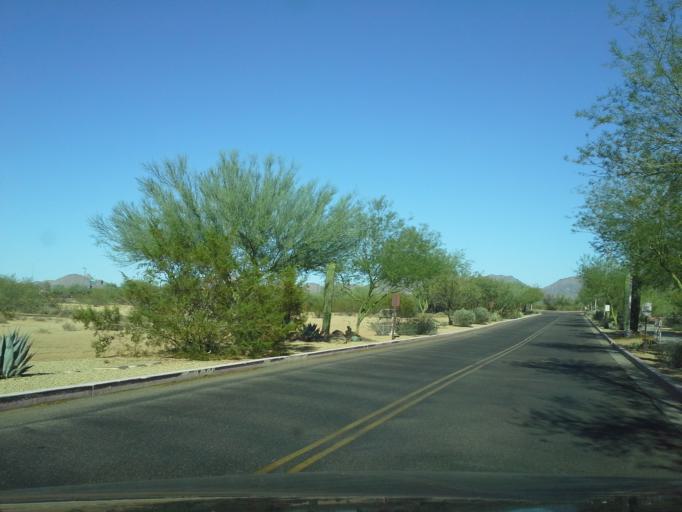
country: US
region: Arizona
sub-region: Maricopa County
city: Paradise Valley
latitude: 33.6620
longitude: -111.9582
